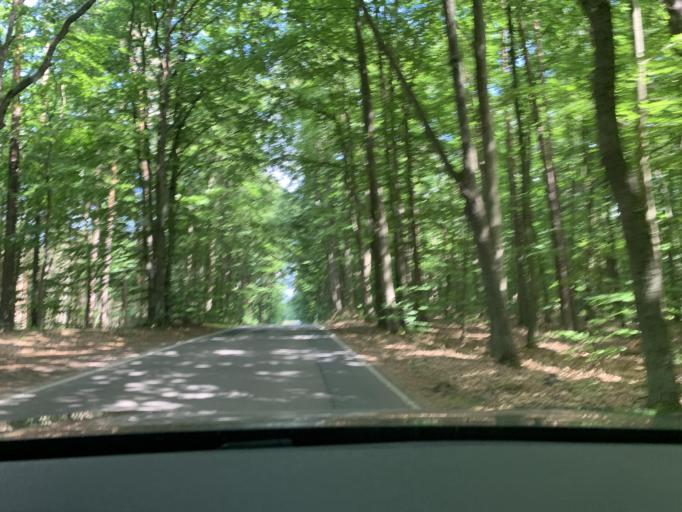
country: DE
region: Brandenburg
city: Rheinsberg
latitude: 53.1841
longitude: 12.8198
